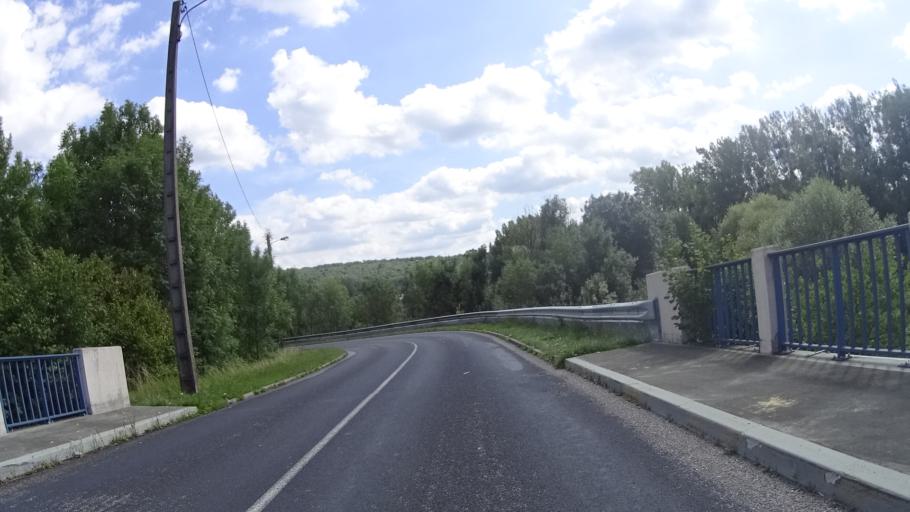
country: FR
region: Lorraine
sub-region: Departement de Meurthe-et-Moselle
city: Foug
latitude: 48.6791
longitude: 5.7891
